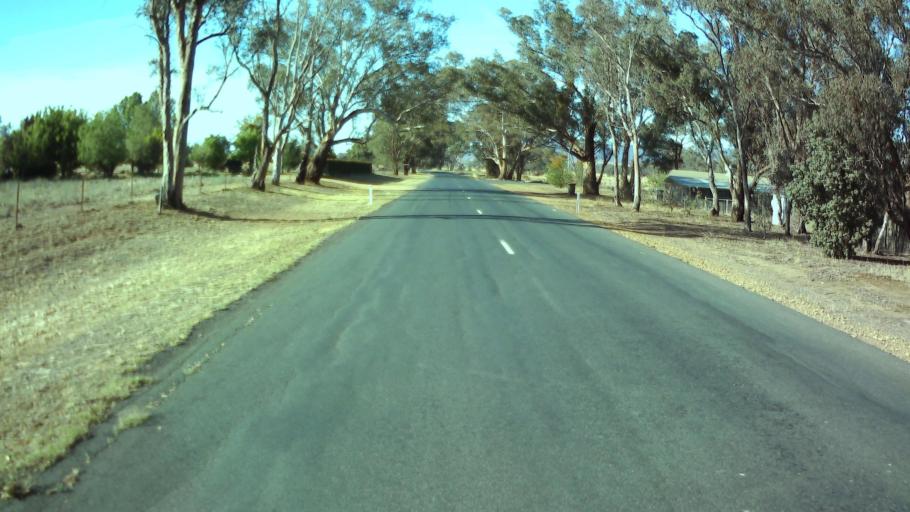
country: AU
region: New South Wales
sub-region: Weddin
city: Grenfell
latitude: -33.9135
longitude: 148.1434
